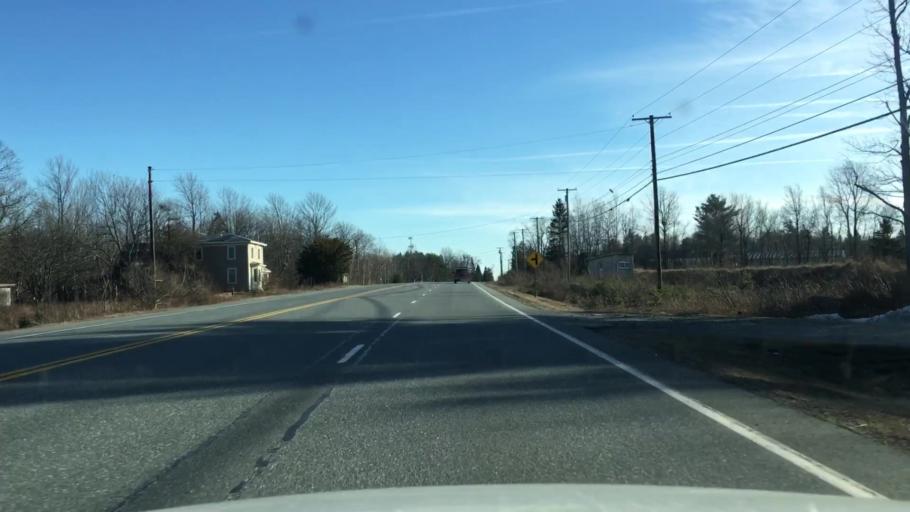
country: US
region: Maine
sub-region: Hancock County
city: Surry
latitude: 44.6255
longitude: -68.5347
